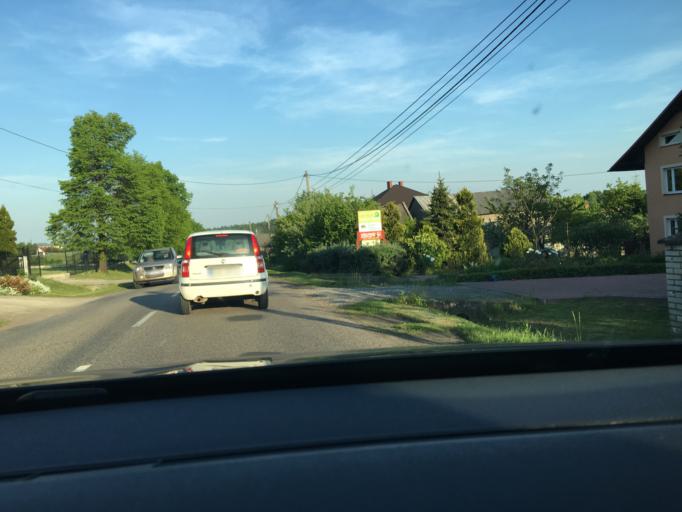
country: PL
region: Lesser Poland Voivodeship
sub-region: Powiat krakowski
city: Saspow
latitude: 50.2288
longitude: 19.7911
